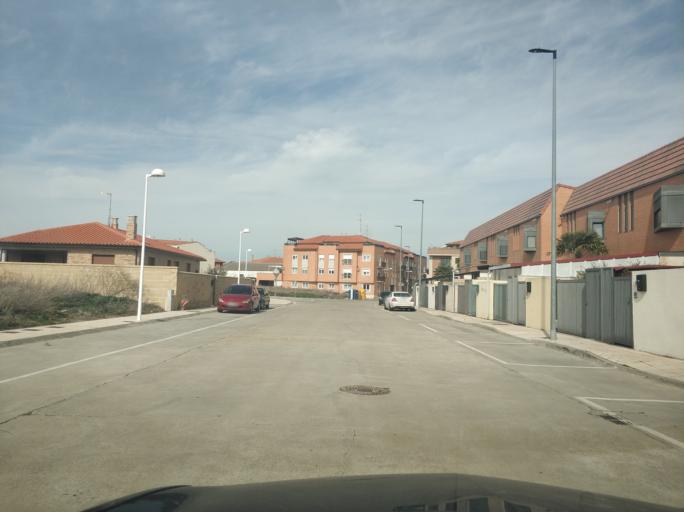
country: ES
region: Castille and Leon
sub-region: Provincia de Salamanca
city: Castellanos de Moriscos
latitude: 41.0162
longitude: -5.5914
